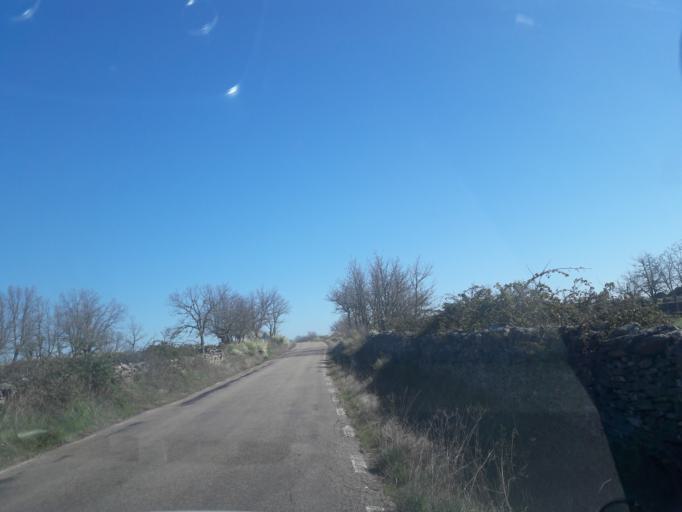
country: ES
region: Castille and Leon
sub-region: Provincia de Salamanca
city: Valsalabroso
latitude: 41.1192
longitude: -6.4833
